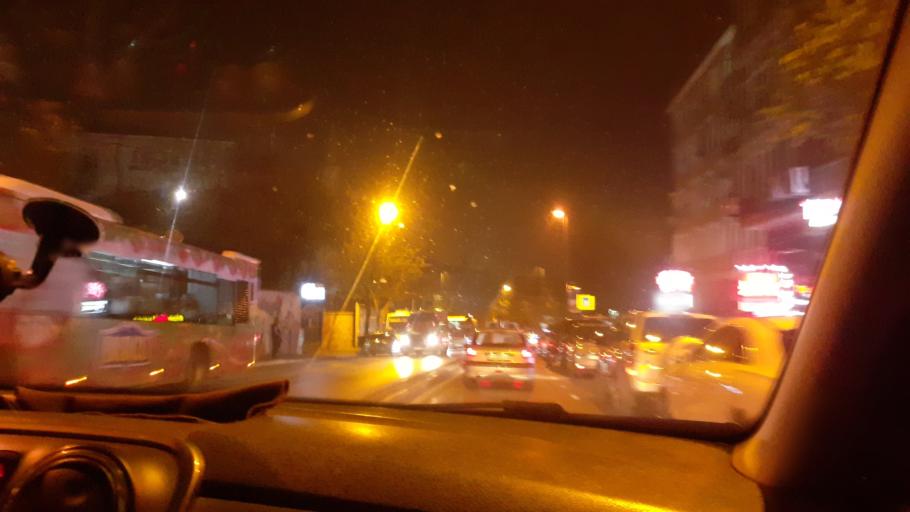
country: TR
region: Istanbul
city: UEskuedar
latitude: 41.0265
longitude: 29.0342
